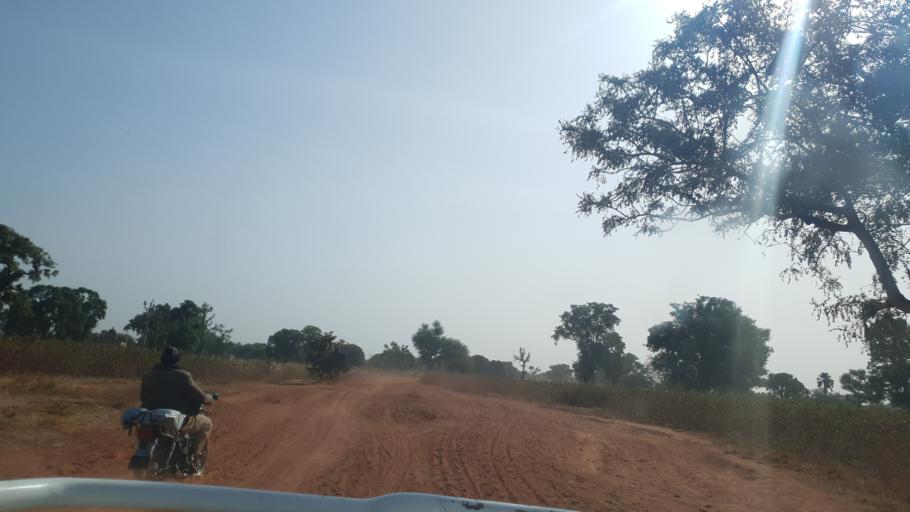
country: ML
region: Koulikoro
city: Dioila
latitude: 12.7074
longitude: -6.7755
